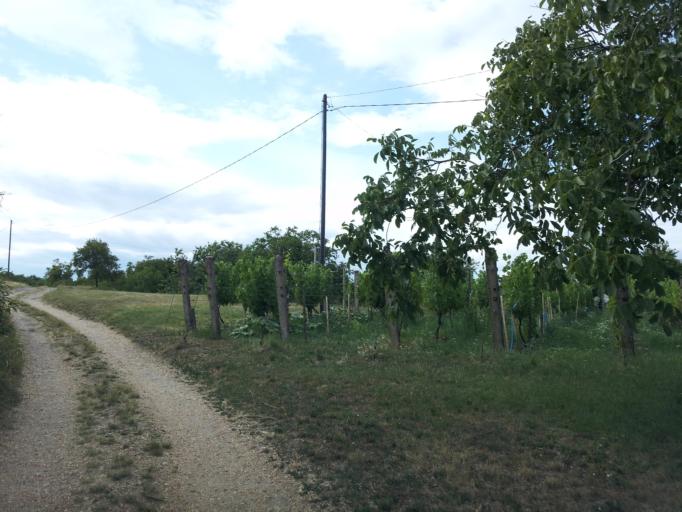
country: HU
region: Vas
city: Janoshaza
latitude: 47.1487
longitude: 17.1031
